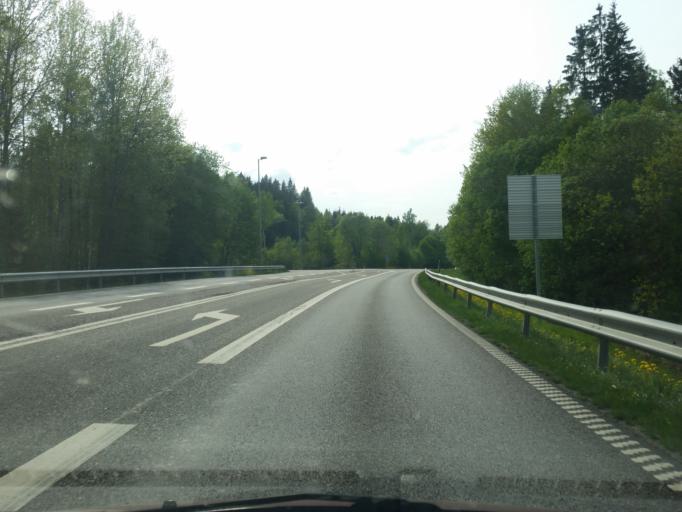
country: SE
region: Vaestra Goetaland
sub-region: Ulricehamns Kommun
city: Ulricehamn
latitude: 57.8022
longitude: 13.3432
